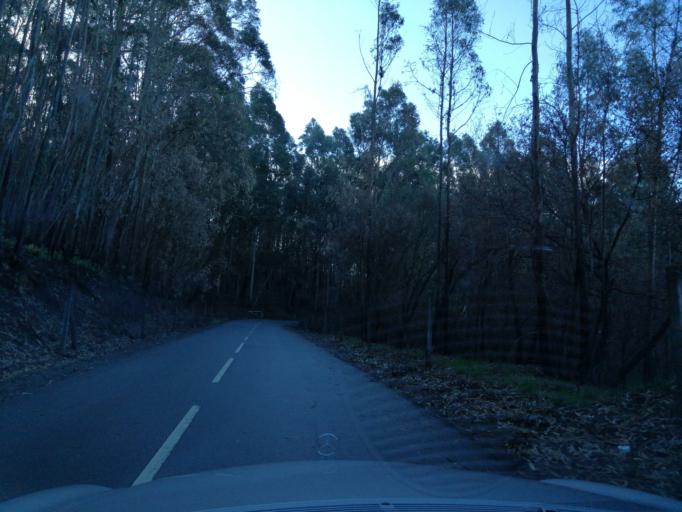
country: PT
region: Braga
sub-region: Braga
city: Braga
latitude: 41.5403
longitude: -8.3899
